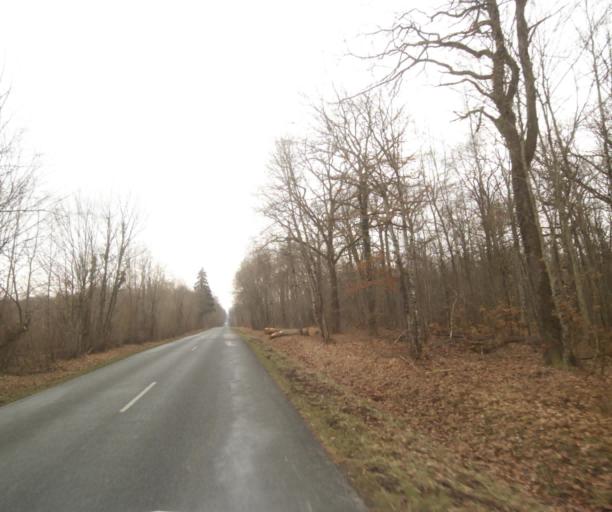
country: FR
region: Champagne-Ardenne
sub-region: Departement de la Haute-Marne
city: Villiers-en-Lieu
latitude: 48.7218
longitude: 4.8750
